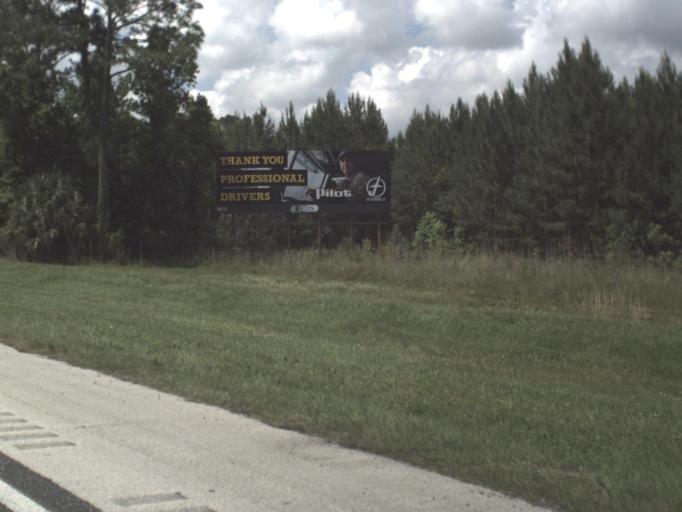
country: US
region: Florida
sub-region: Saint Johns County
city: Saint Augustine
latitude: 29.9535
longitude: -81.4417
